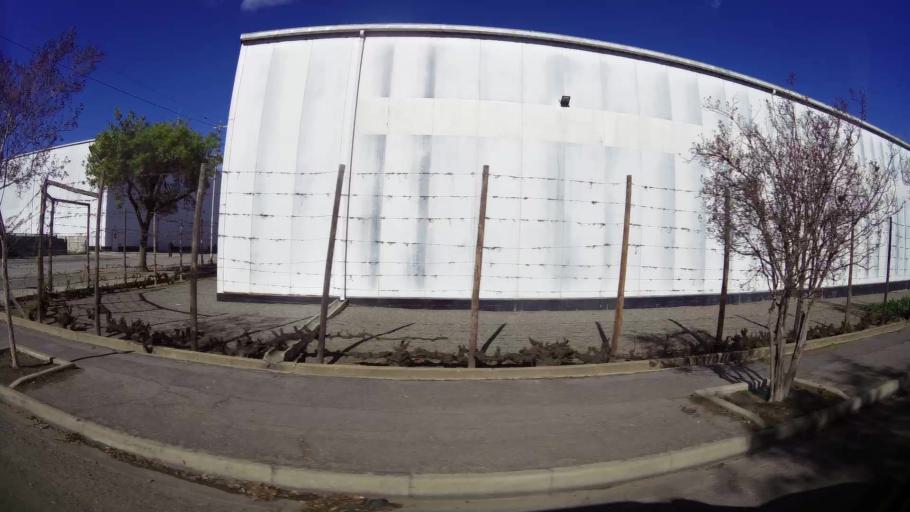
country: ZA
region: Western Cape
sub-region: Cape Winelands District Municipality
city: Ashton
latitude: -33.8085
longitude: 19.8798
